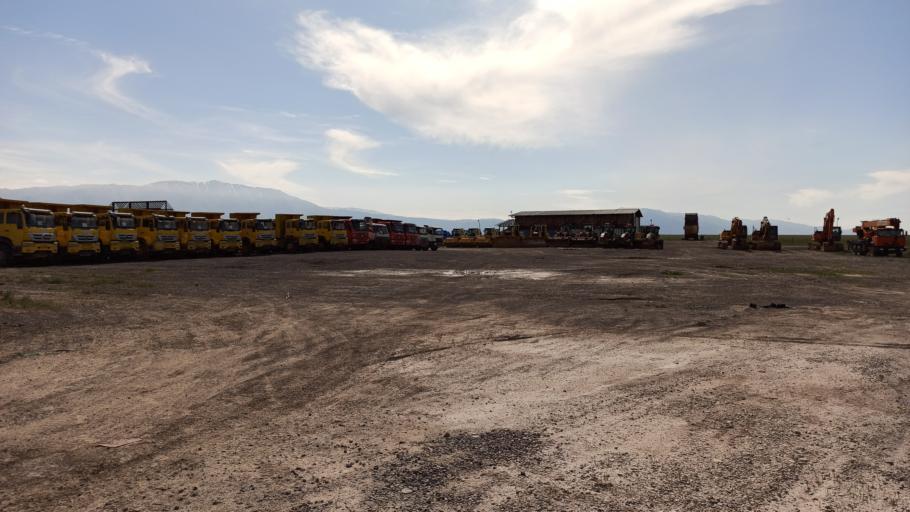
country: KG
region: Chuy
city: Bystrovka
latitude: 43.3237
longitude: 75.6847
